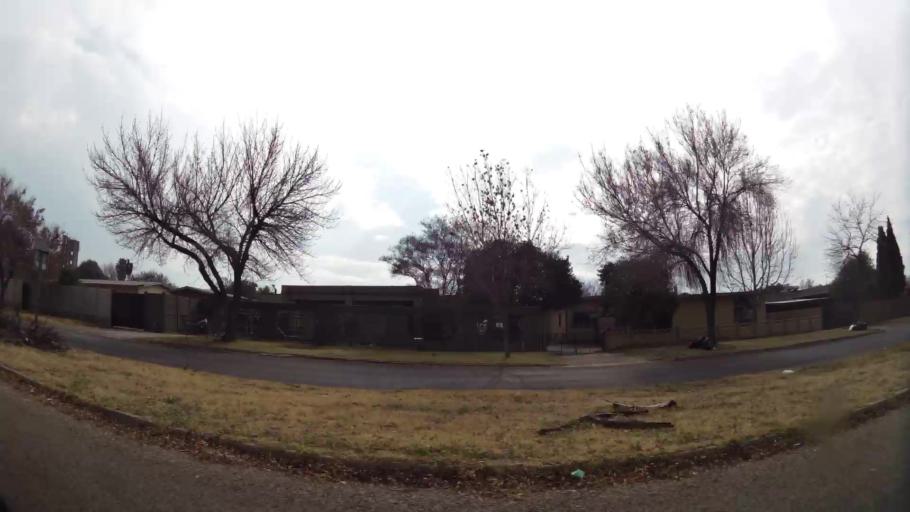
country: ZA
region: Gauteng
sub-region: Sedibeng District Municipality
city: Vanderbijlpark
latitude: -26.6839
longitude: 27.8368
